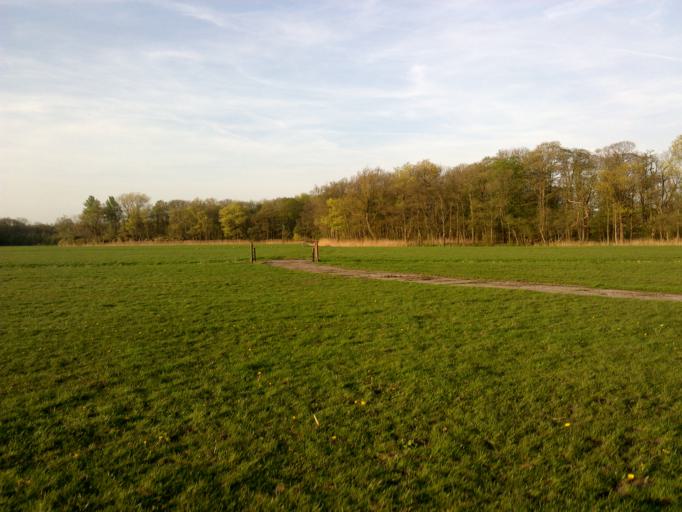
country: NL
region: South Holland
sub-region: Gemeente Lisse
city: Lisse
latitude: 52.2688
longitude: 4.5366
